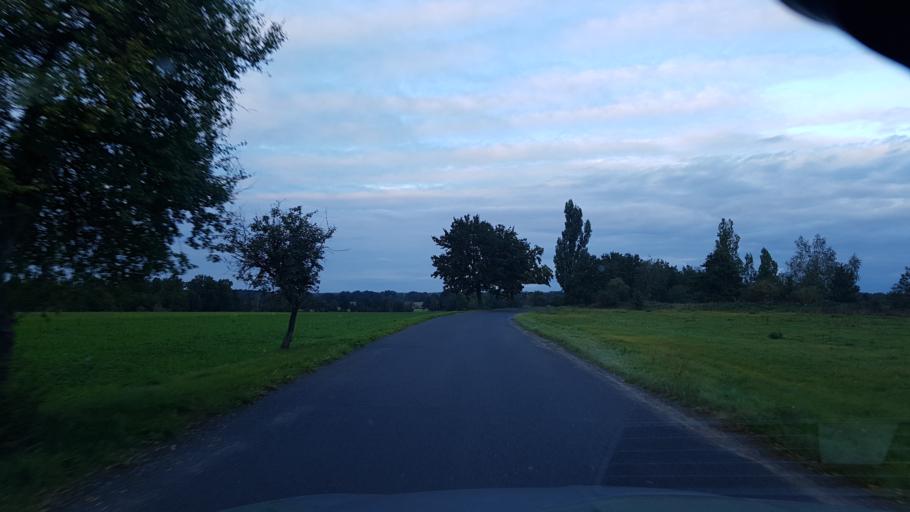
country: DE
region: Saxony
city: Ebersbach
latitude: 51.2727
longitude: 13.6025
